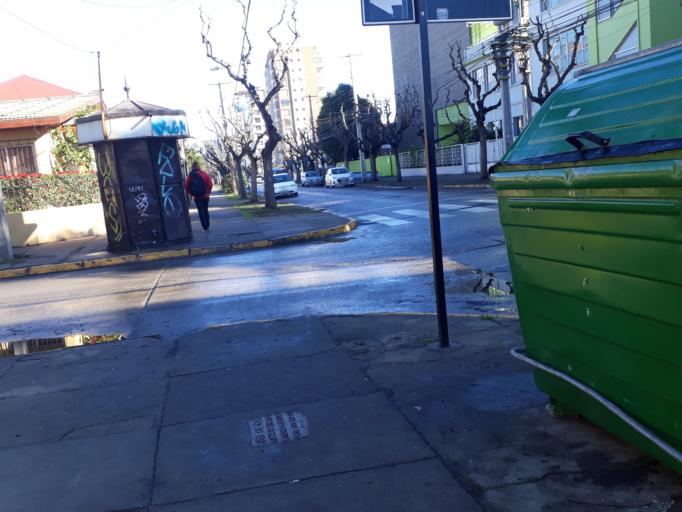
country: CL
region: Valparaiso
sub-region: Provincia de Valparaiso
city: Vina del Mar
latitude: -33.0139
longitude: -71.5457
